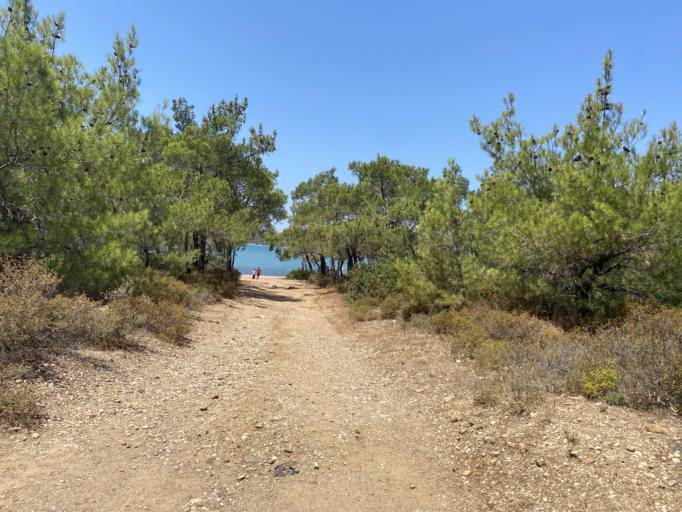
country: TR
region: Balikesir
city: Ayvalik
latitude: 39.2934
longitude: 26.6483
